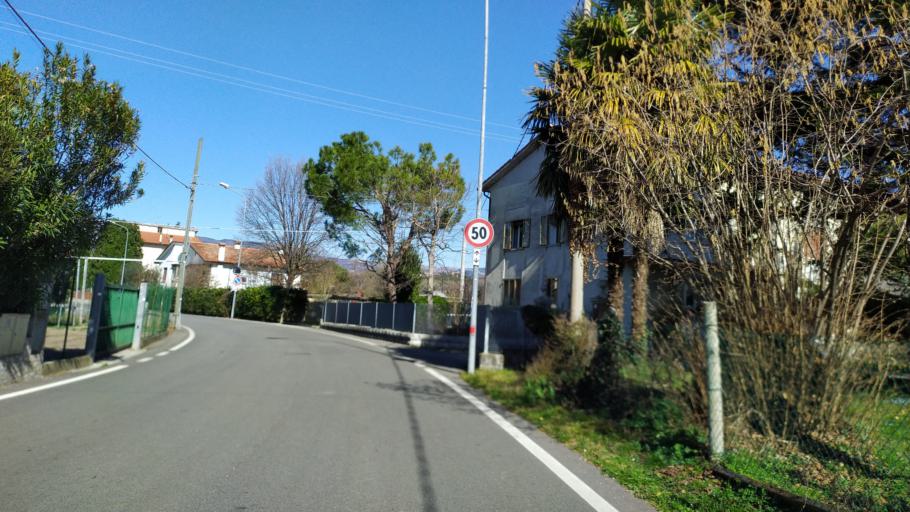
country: IT
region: Veneto
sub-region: Provincia di Vicenza
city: Breganze
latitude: 45.7034
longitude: 11.5527
